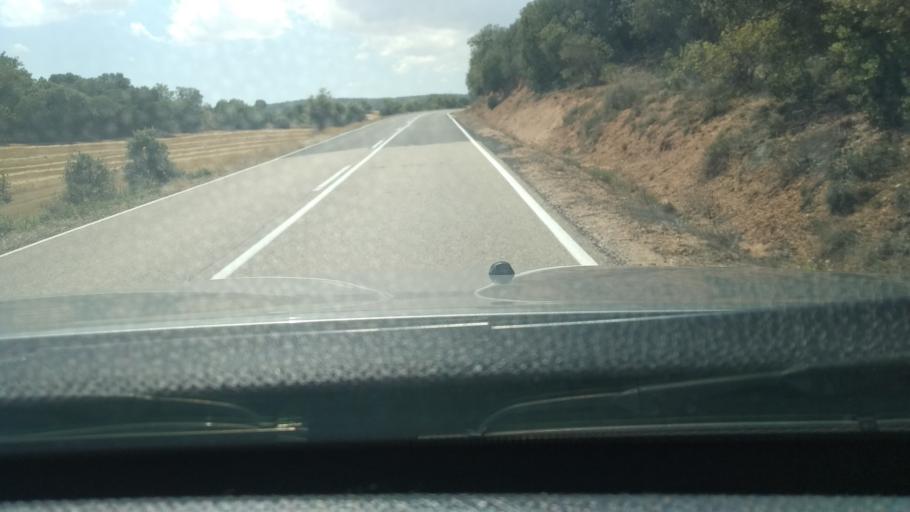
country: ES
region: Castille and Leon
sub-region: Provincia de Burgos
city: Quintanilla de la Mata
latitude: 41.9857
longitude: -3.7801
